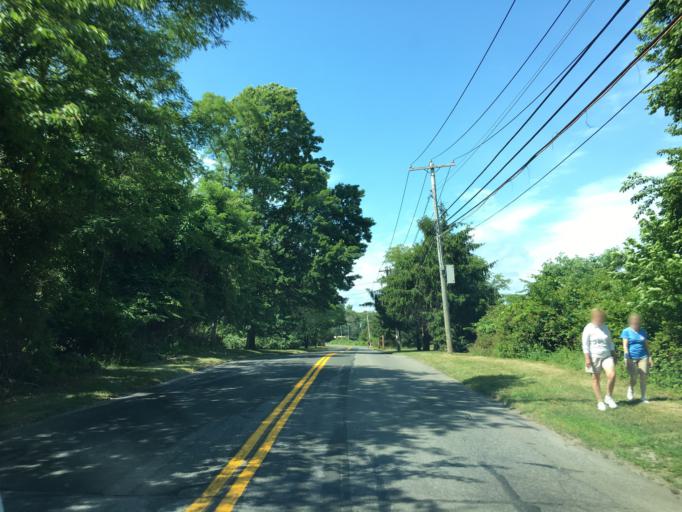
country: US
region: New York
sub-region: Suffolk County
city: Shelter Island Heights
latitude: 41.0598
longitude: -72.3680
